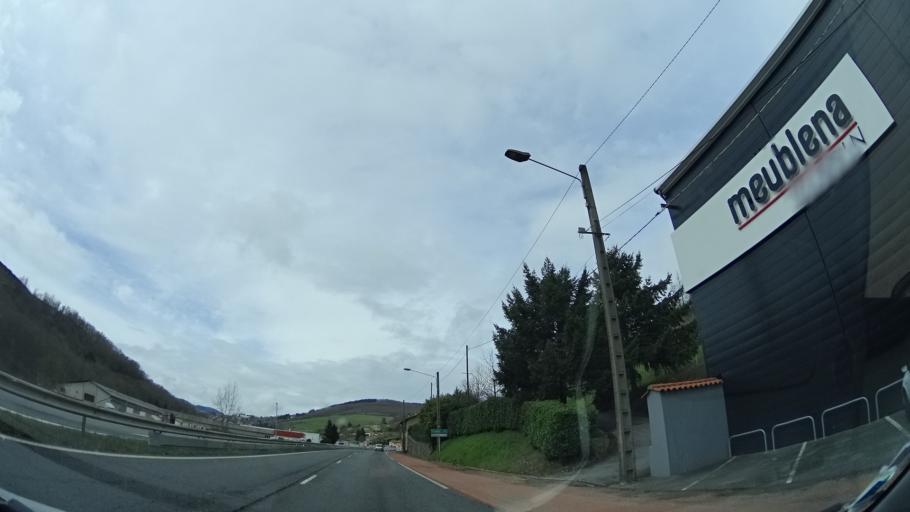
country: FR
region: Rhone-Alpes
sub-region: Departement du Rhone
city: Pontcharra-sur-Turdine
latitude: 45.8811
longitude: 4.4731
